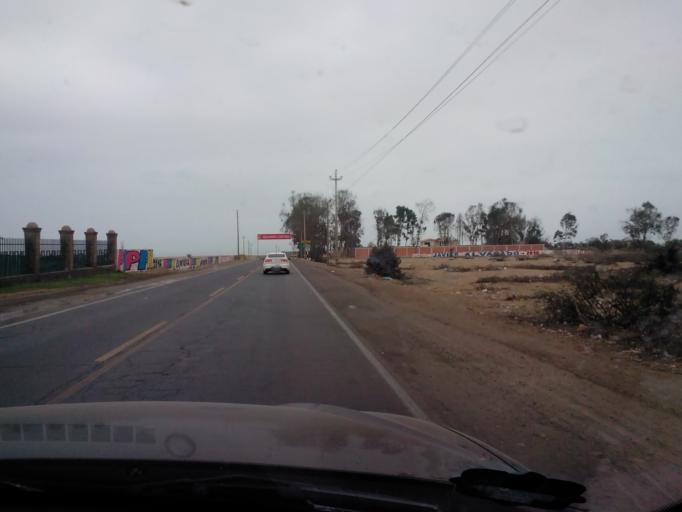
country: PE
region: Ica
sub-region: Provincia de Chincha
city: Sunampe
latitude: -13.4130
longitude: -76.1817
